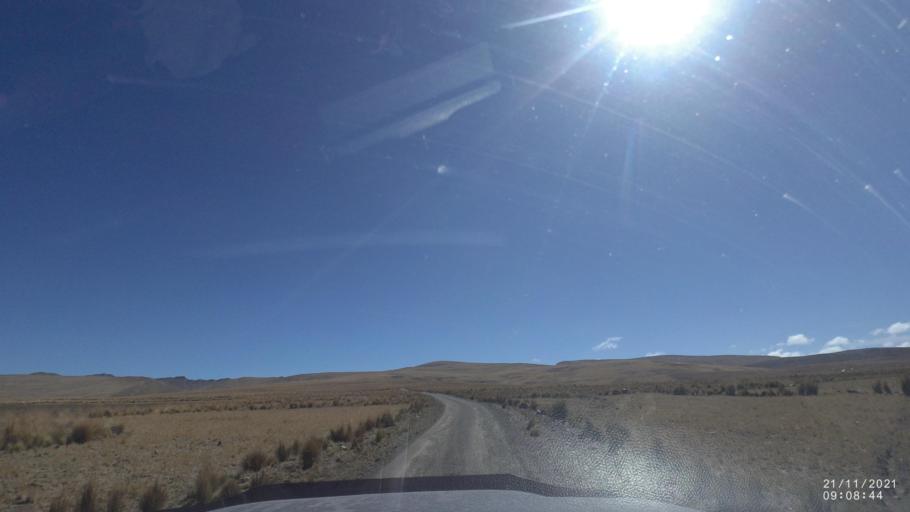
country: BO
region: Cochabamba
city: Cochabamba
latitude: -17.1610
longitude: -66.2661
